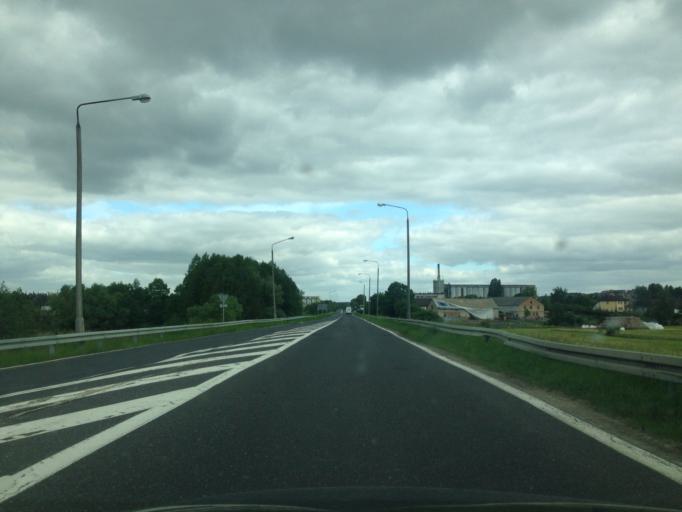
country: PL
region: Kujawsko-Pomorskie
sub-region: Powiat swiecki
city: Swiecie
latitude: 53.3919
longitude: 18.4063
